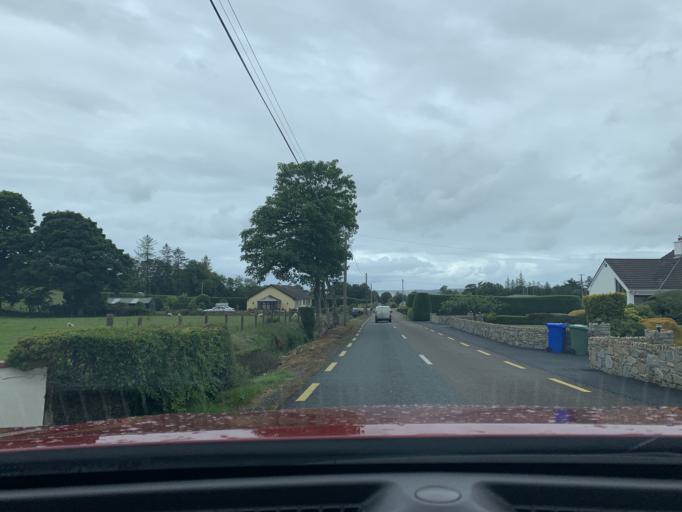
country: IE
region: Connaught
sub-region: Sligo
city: Sligo
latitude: 54.3147
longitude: -8.4736
